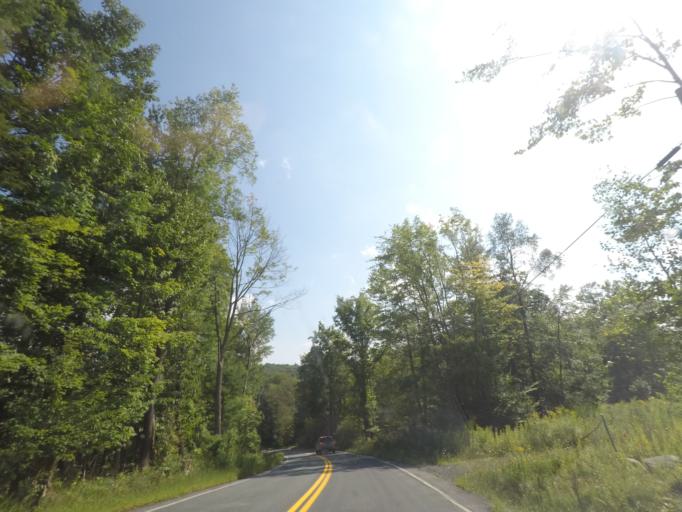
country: US
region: New York
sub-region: Rensselaer County
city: Poestenkill
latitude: 42.7116
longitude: -73.5091
